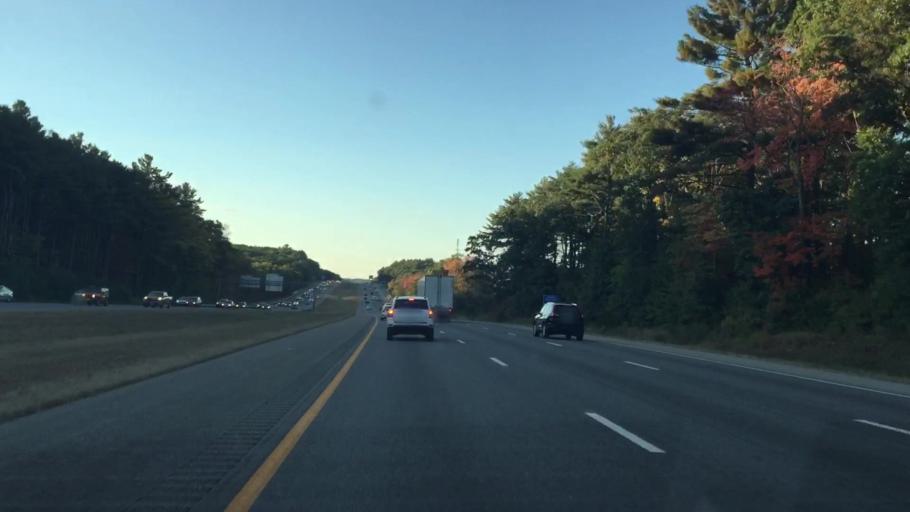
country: US
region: Massachusetts
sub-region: Middlesex County
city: Burlington
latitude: 42.4846
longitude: -71.2256
